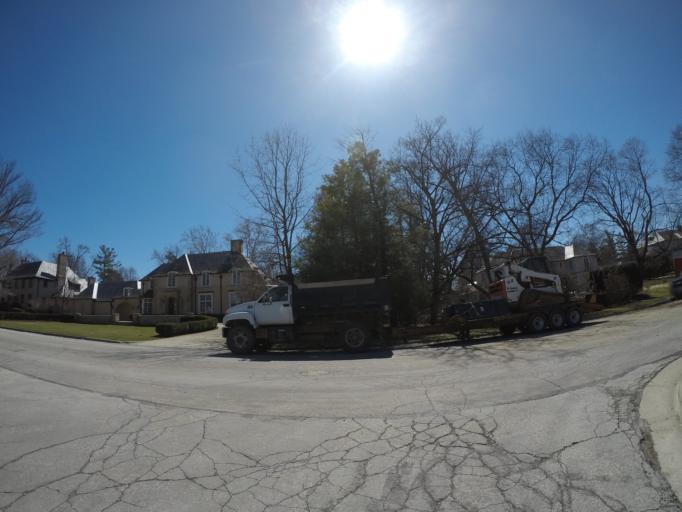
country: US
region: Ohio
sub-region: Franklin County
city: Upper Arlington
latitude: 40.0097
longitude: -83.0733
